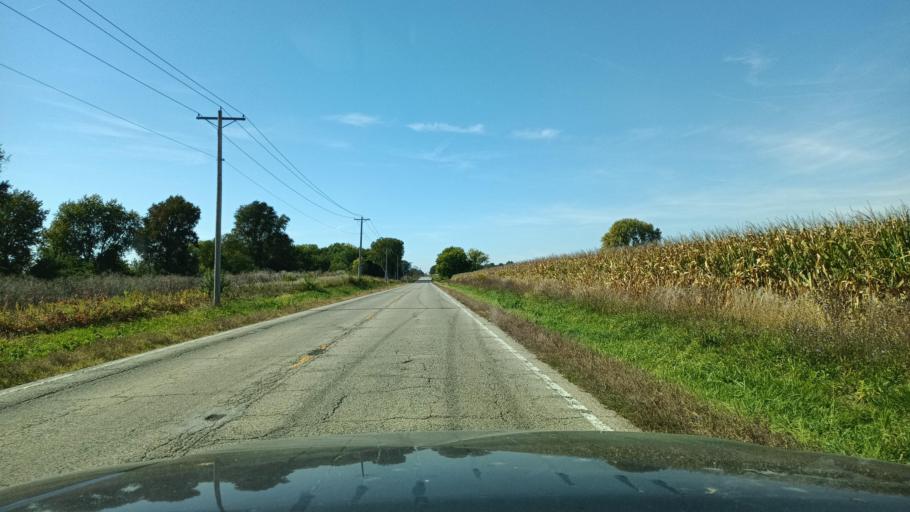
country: US
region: Illinois
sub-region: Champaign County
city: Mahomet
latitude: 40.2094
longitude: -88.4888
